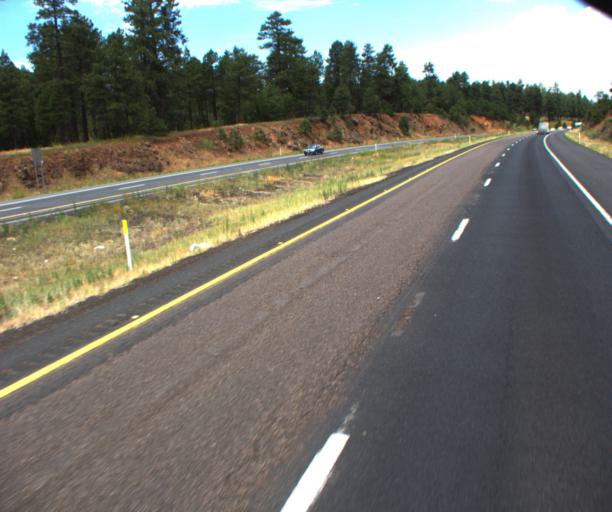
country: US
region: Arizona
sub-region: Coconino County
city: Mountainaire
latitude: 35.0767
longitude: -111.6851
